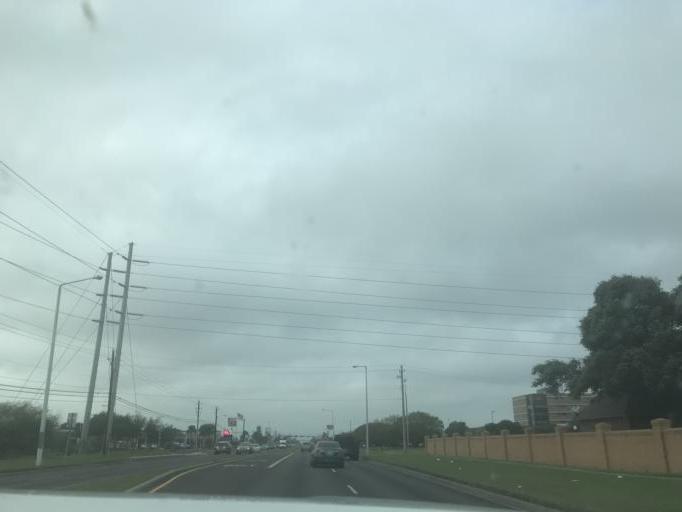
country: US
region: Texas
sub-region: Nueces County
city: Corpus Christi
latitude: 27.6816
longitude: -97.3760
